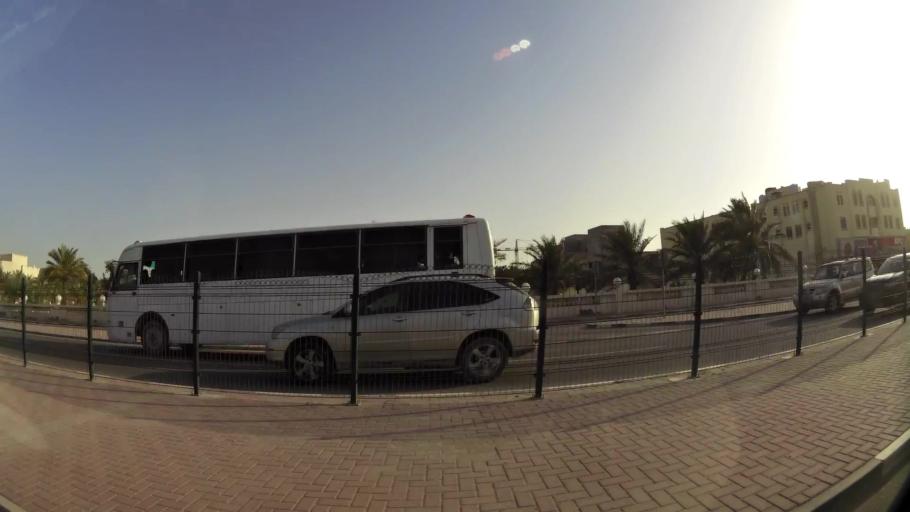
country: QA
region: Baladiyat ar Rayyan
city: Ar Rayyan
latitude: 25.3284
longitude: 51.4520
